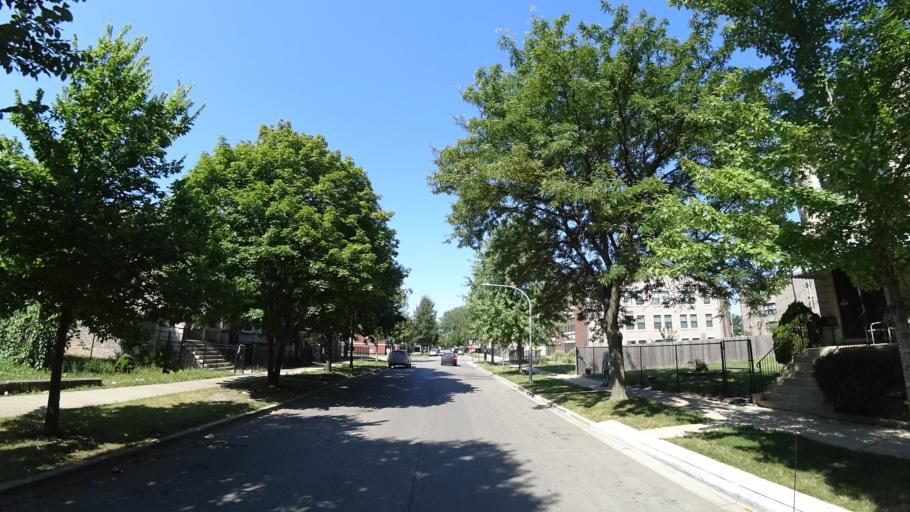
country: US
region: Illinois
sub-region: Cook County
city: Cicero
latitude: 41.8717
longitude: -87.7172
